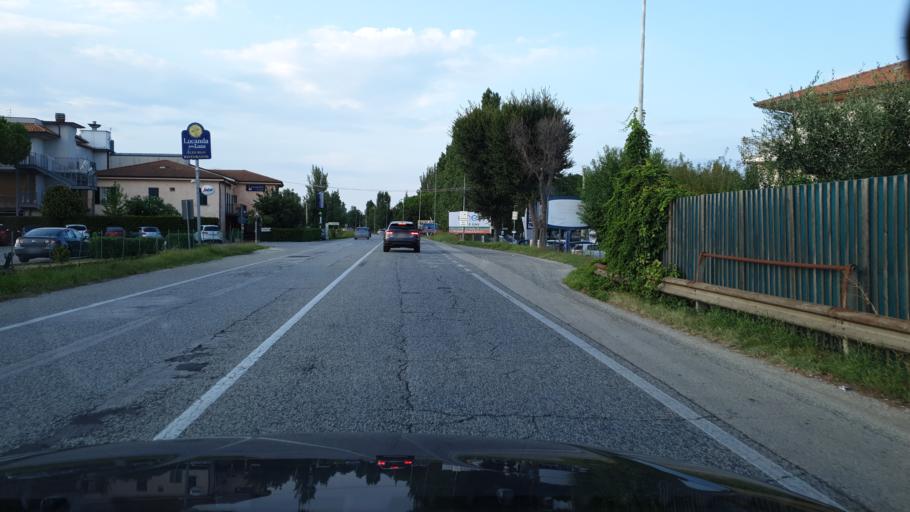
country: IT
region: Emilia-Romagna
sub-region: Provincia di Rimini
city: Riccione
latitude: 44.0101
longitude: 12.6332
